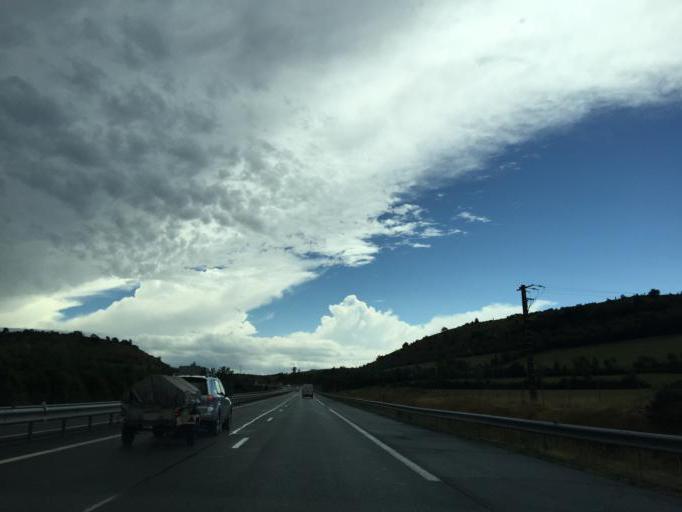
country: FR
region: Midi-Pyrenees
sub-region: Departement de l'Aveyron
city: Severac-le-Chateau
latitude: 44.3219
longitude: 3.0909
